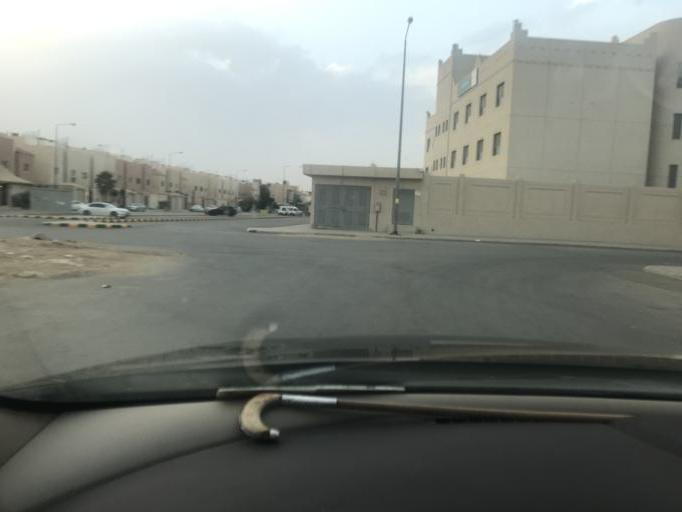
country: SA
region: Ar Riyad
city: Riyadh
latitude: 24.7269
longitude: 46.7465
